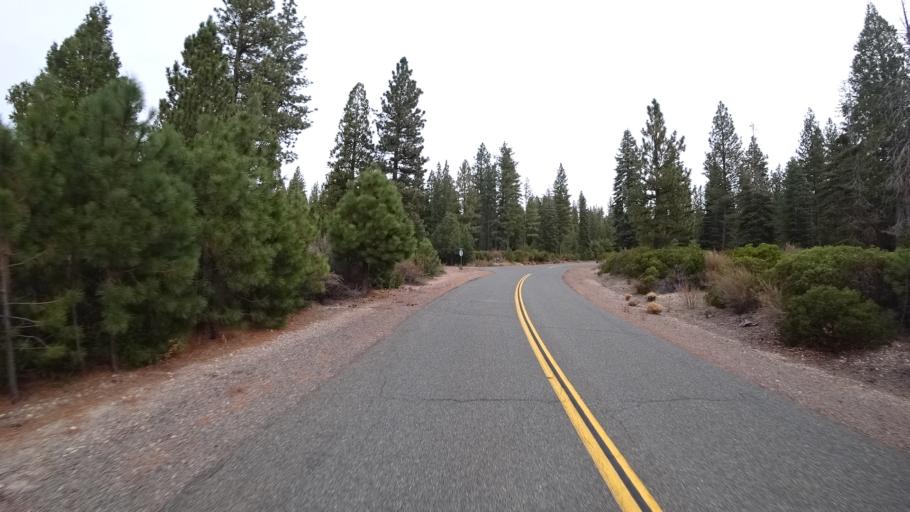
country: US
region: California
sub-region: Siskiyou County
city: Weed
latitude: 41.4124
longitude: -122.3712
